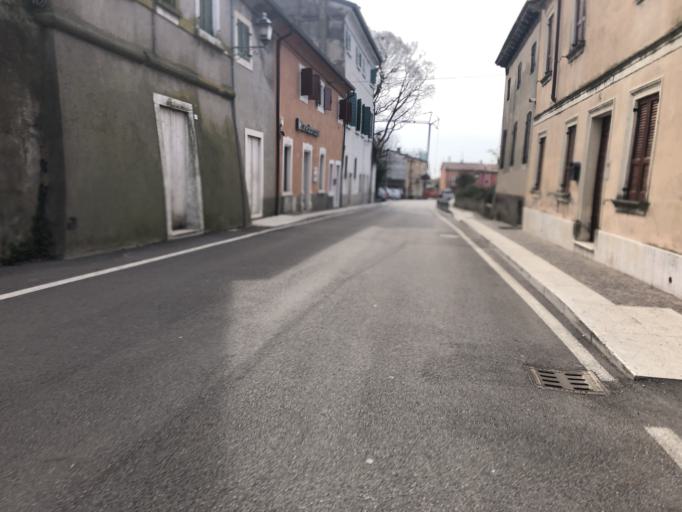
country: IT
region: Veneto
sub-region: Provincia di Verona
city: San Giorgio in Salici
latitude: 45.4264
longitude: 10.7873
